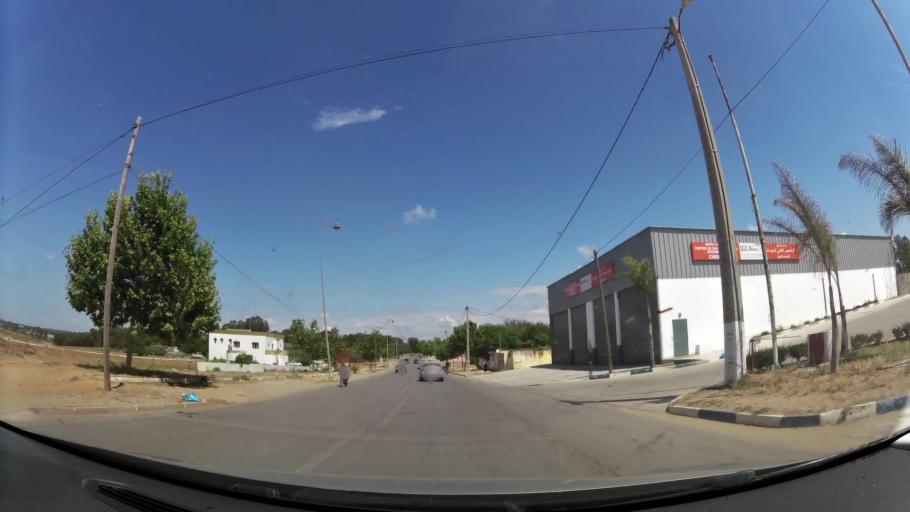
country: MA
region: Gharb-Chrarda-Beni Hssen
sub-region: Kenitra Province
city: Kenitra
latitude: 34.2332
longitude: -6.5405
